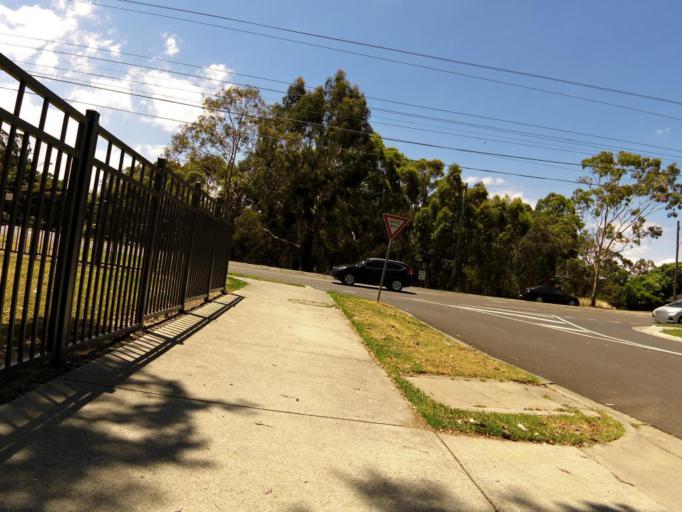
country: AU
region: Victoria
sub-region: Monash
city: Notting Hill
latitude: -37.8860
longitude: 145.1363
